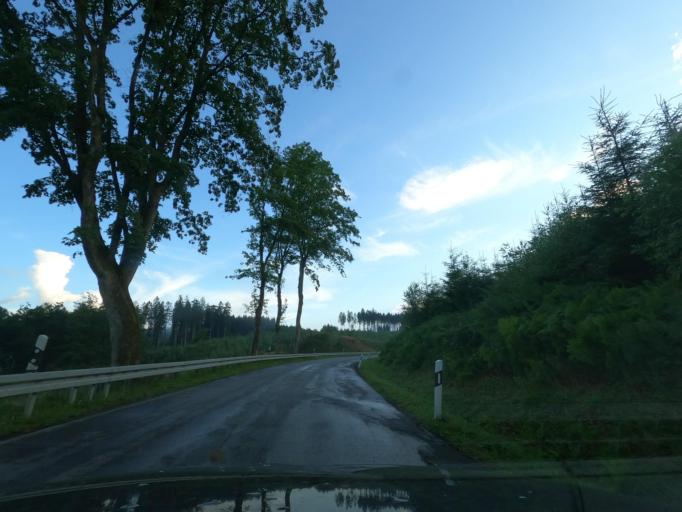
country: DE
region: North Rhine-Westphalia
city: Plettenberg
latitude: 51.2613
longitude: 7.9294
